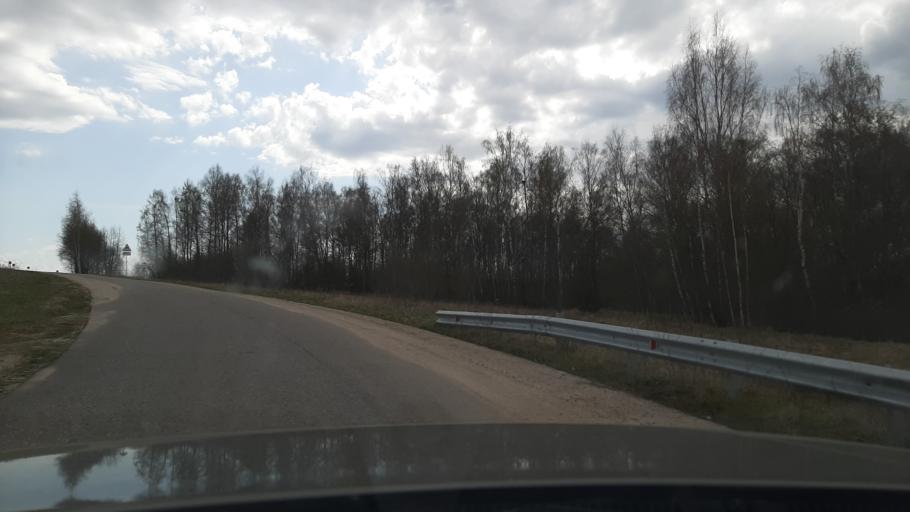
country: RU
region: Ivanovo
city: Furmanov
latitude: 57.3146
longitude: 41.1641
